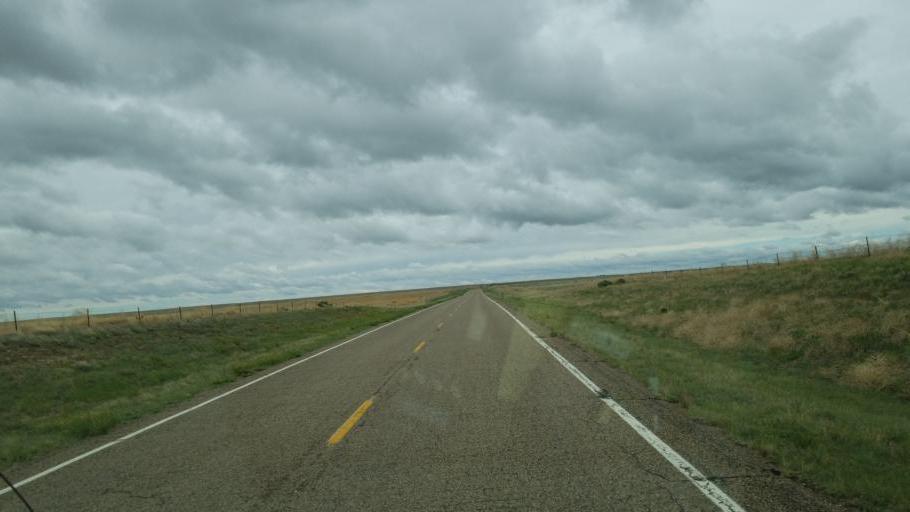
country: US
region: Colorado
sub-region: Lincoln County
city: Hugo
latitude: 38.8509
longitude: -103.6017
